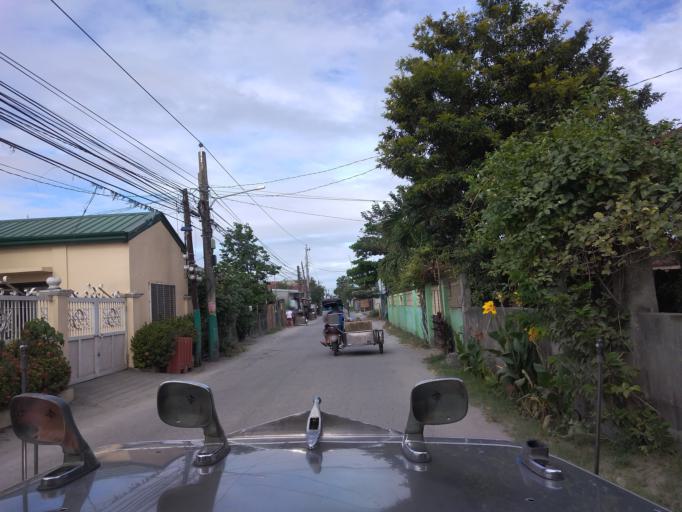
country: PH
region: Central Luzon
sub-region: Province of Pampanga
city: Mexico
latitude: 15.0690
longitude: 120.7156
